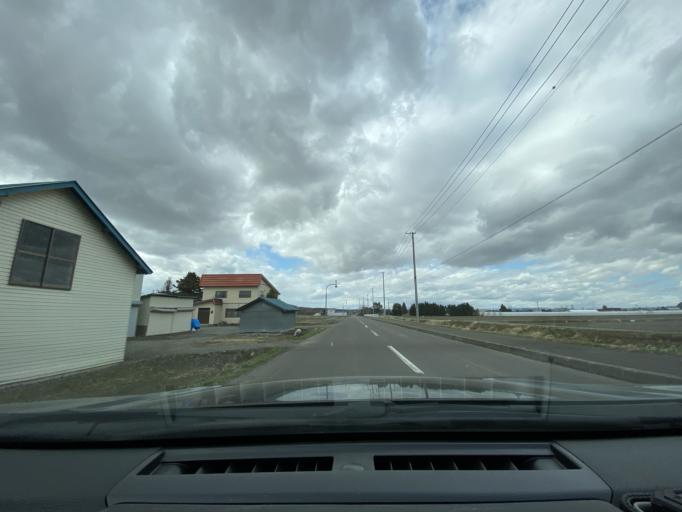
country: JP
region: Hokkaido
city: Nayoro
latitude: 44.1300
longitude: 142.4914
